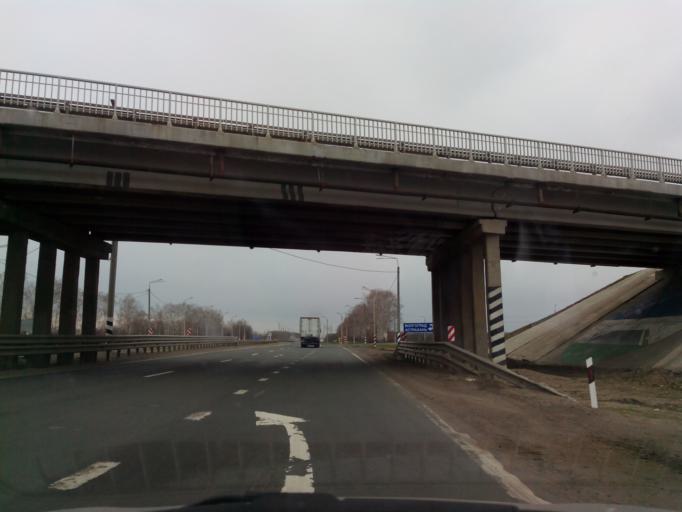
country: RU
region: Tambov
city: Komsomolets
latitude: 52.7336
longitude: 41.2962
